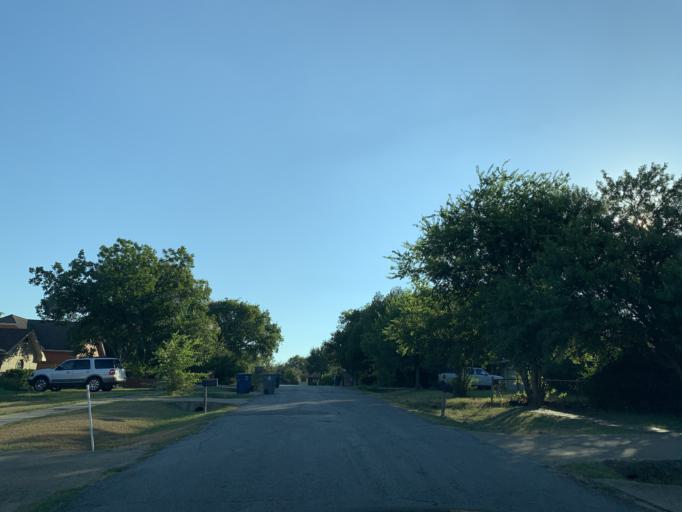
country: US
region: Texas
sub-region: Dallas County
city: Hutchins
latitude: 32.6732
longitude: -96.7776
